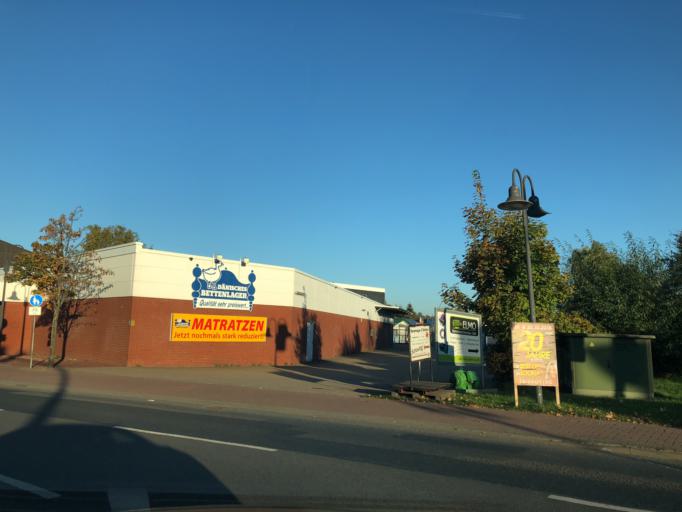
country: DE
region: Lower Saxony
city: Friesoythe
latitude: 53.0239
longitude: 7.8621
